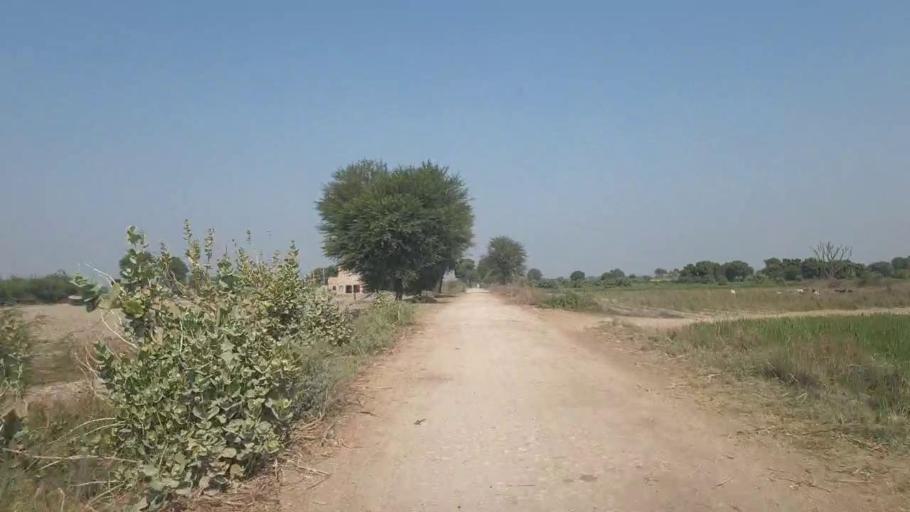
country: PK
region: Sindh
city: Tando Allahyar
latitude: 25.4492
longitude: 68.8500
